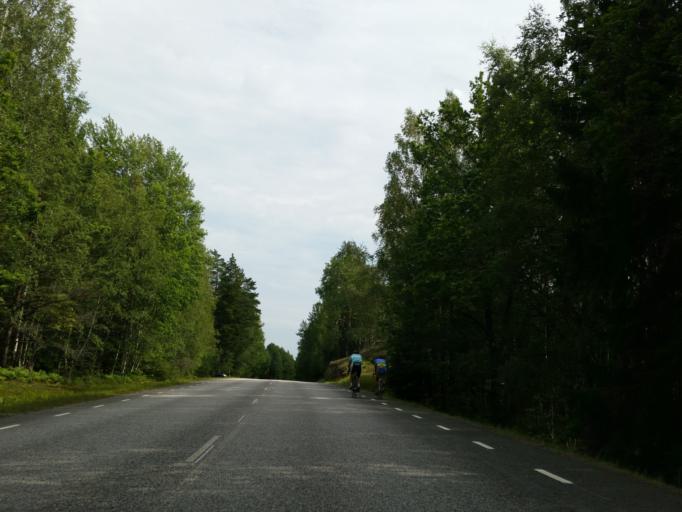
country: SE
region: Soedermanland
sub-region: Strangnas Kommun
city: Mariefred
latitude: 59.2326
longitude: 17.2067
